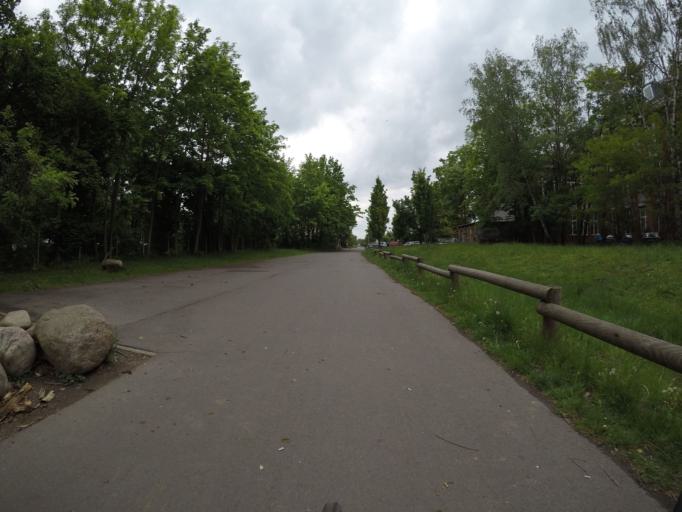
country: DE
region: Berlin
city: Lichtenberg
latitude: 52.5269
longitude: 13.5044
